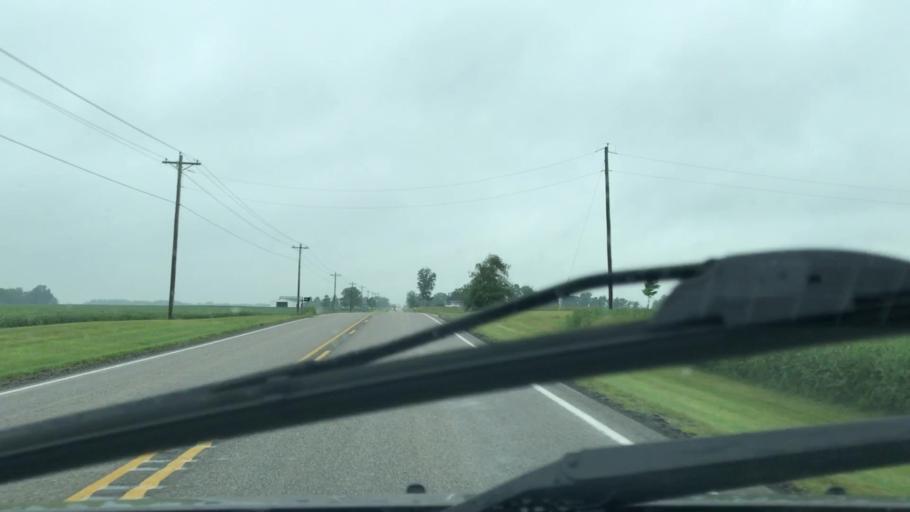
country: US
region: Indiana
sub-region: Boone County
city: Lebanon
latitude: 40.1264
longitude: -86.4448
